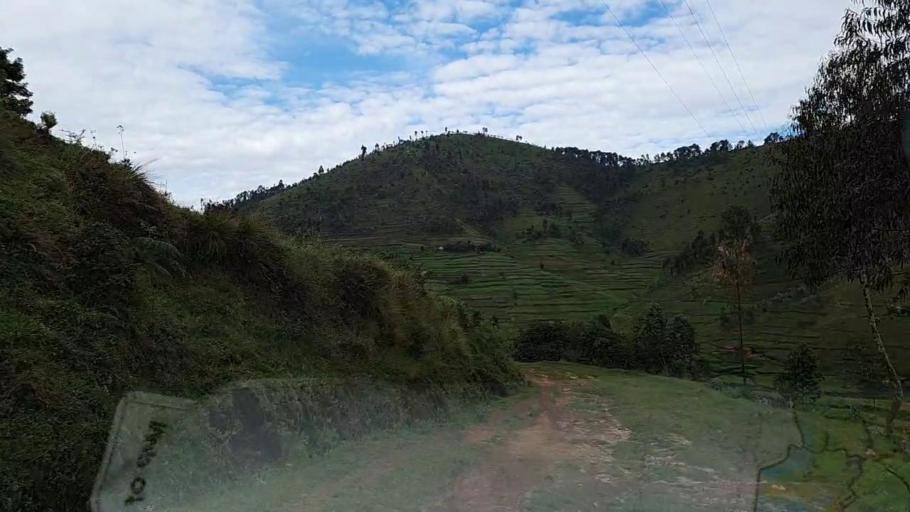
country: RW
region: Southern Province
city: Nzega
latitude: -2.4065
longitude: 29.4968
